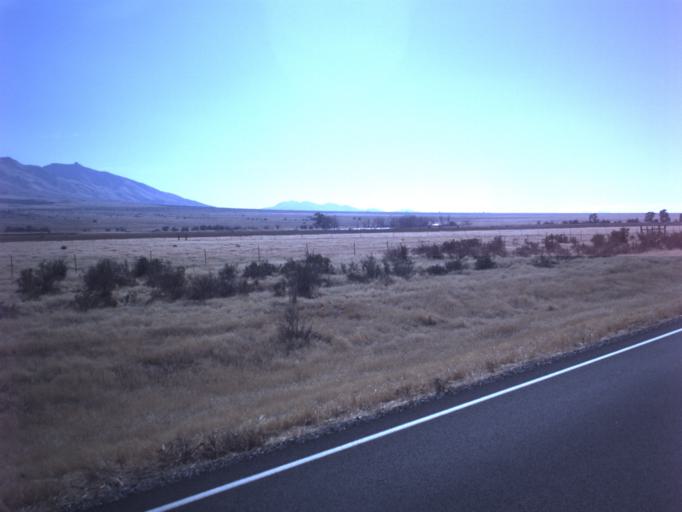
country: US
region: Utah
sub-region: Tooele County
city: Grantsville
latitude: 40.4679
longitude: -112.7467
